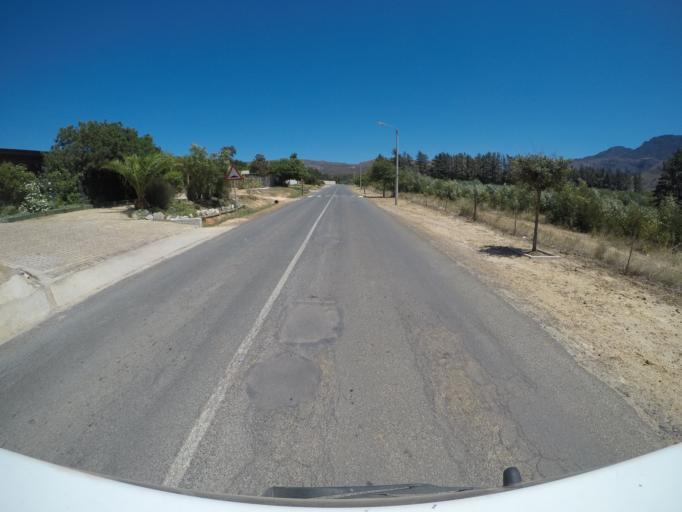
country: ZA
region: Western Cape
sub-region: Overberg District Municipality
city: Hermanus
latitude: -34.2237
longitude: 19.2021
